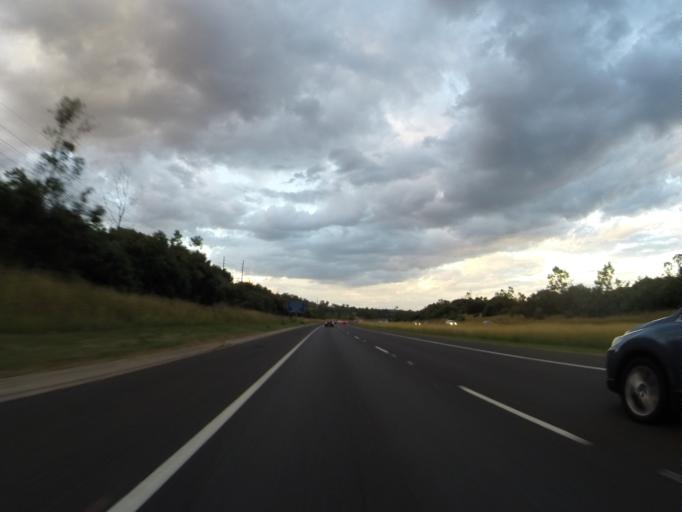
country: AU
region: New South Wales
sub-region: Campbelltown Municipality
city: Glen Alpine
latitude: -34.0705
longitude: 150.7782
